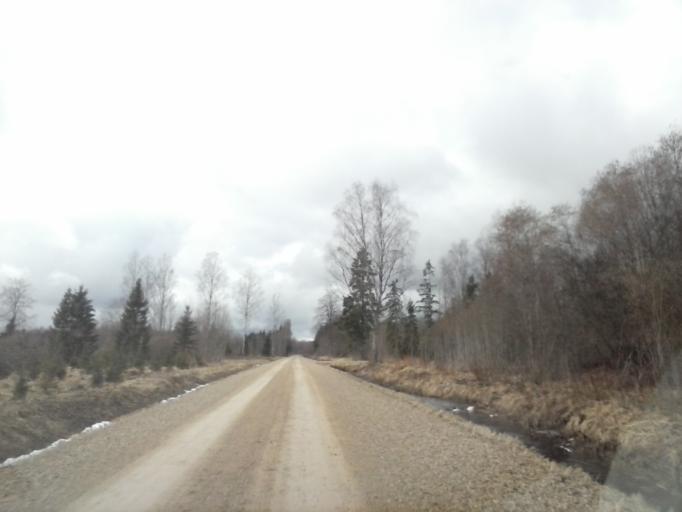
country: EE
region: Jogevamaa
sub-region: Mustvee linn
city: Mustvee
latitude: 59.0950
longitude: 26.8315
